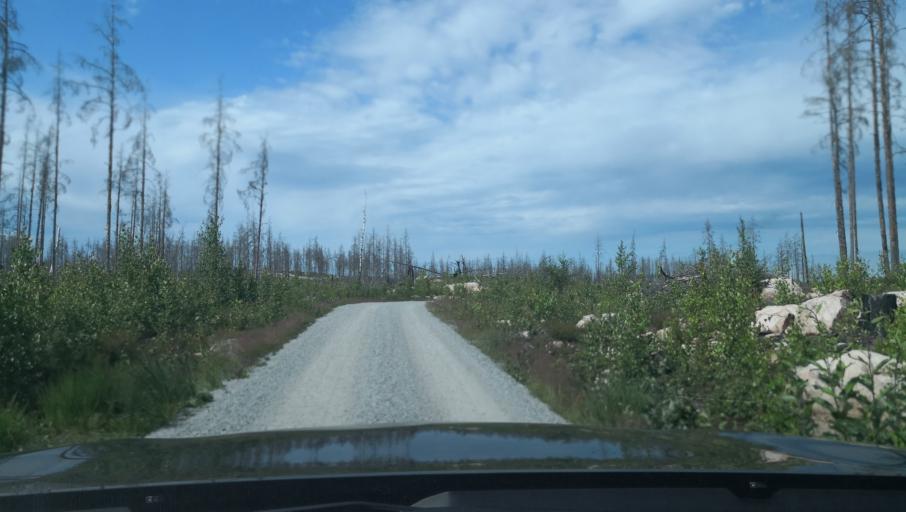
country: SE
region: Vaestmanland
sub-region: Surahammars Kommun
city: Ramnas
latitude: 59.9315
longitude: 16.1888
